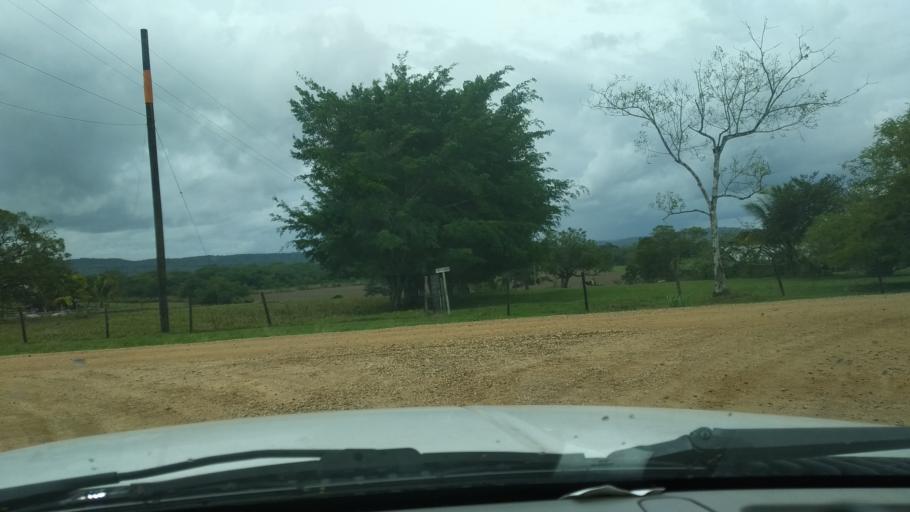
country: BZ
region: Cayo
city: San Ignacio
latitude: 17.2265
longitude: -88.9877
